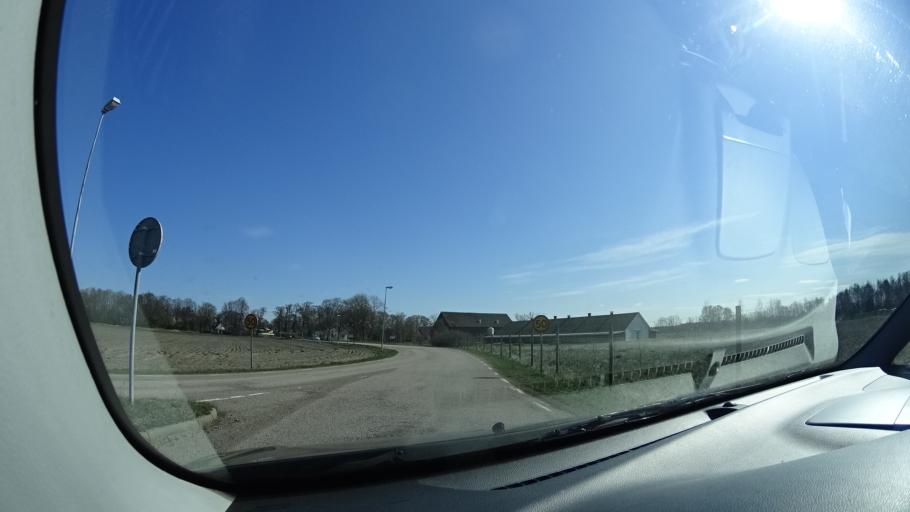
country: SE
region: Skane
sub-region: Hoganas Kommun
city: Hoganas
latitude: 56.2165
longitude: 12.6654
